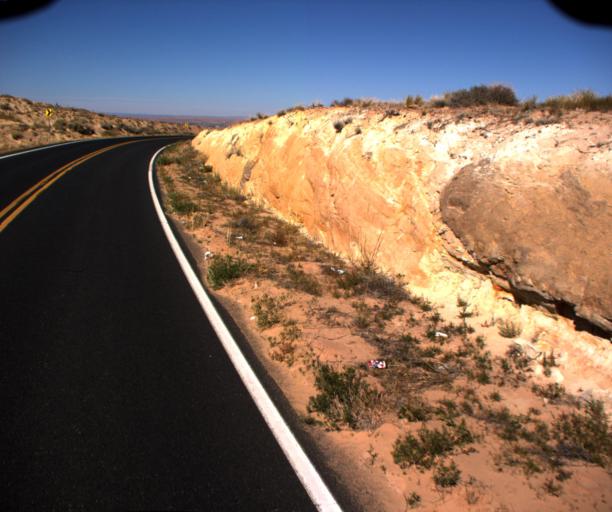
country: US
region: Arizona
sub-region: Coconino County
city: Tuba City
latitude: 36.0371
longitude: -111.1851
